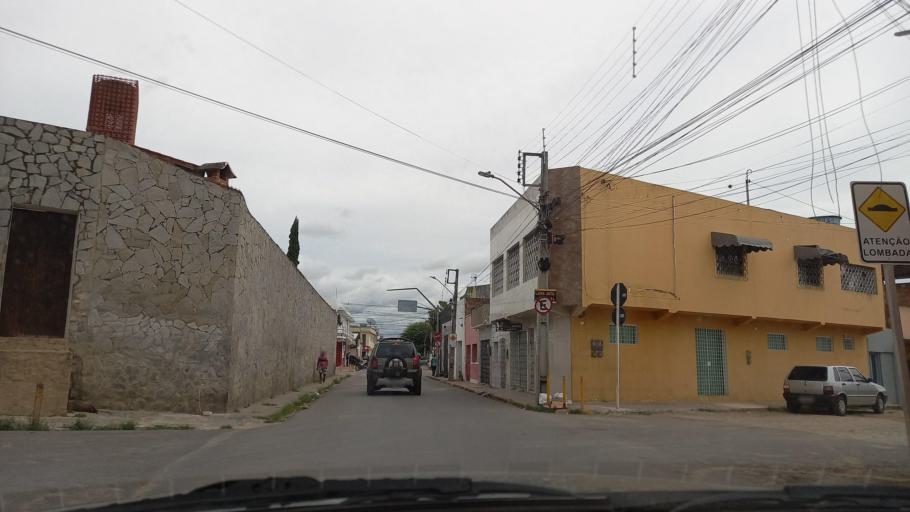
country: BR
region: Pernambuco
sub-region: Gravata
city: Gravata
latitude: -8.2012
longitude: -35.5702
